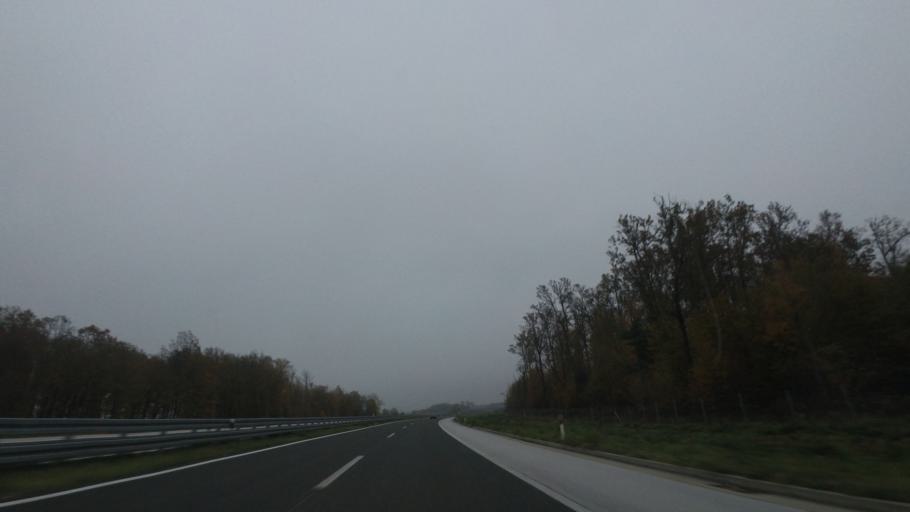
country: HR
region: Zagrebacka
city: Turopolje
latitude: 45.6124
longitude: 16.1160
